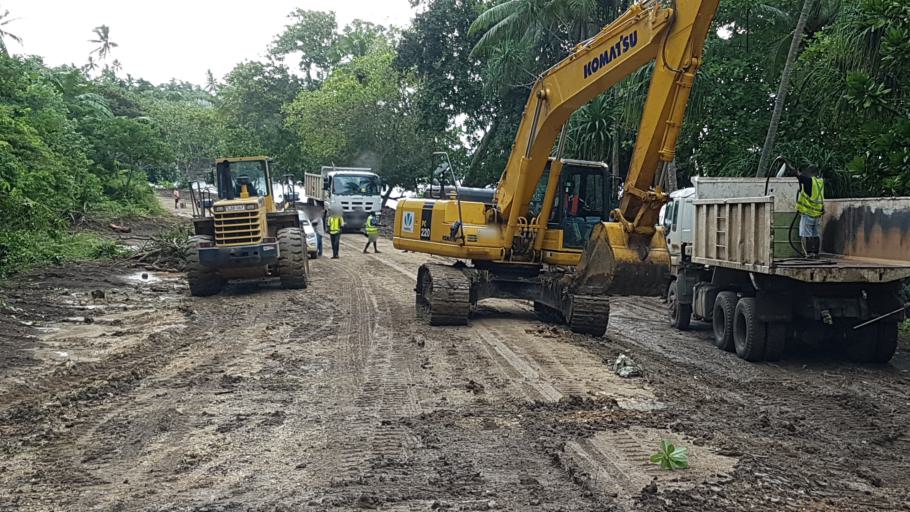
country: PG
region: Milne Bay
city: Alotau
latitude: -10.2986
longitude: 150.7619
